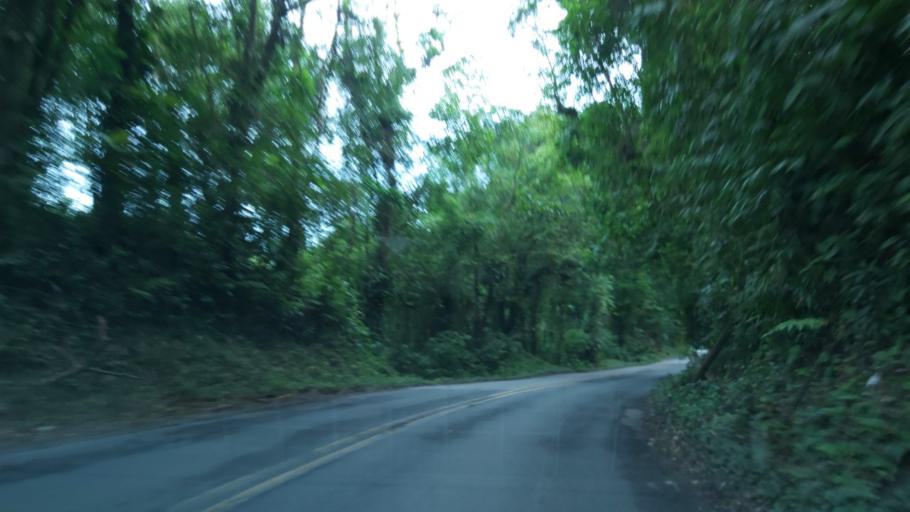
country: BR
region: Sao Paulo
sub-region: Juquia
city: Juquia
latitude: -24.0735
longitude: -47.6034
